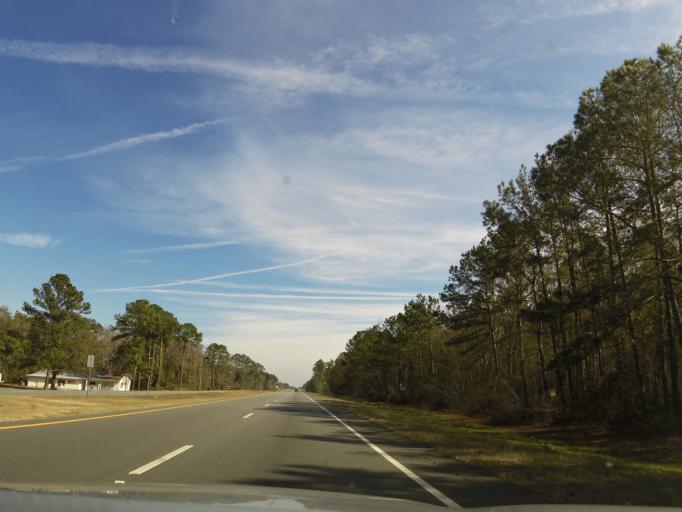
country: US
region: Georgia
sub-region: Brantley County
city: Nahunta
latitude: 31.2146
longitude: -81.9010
